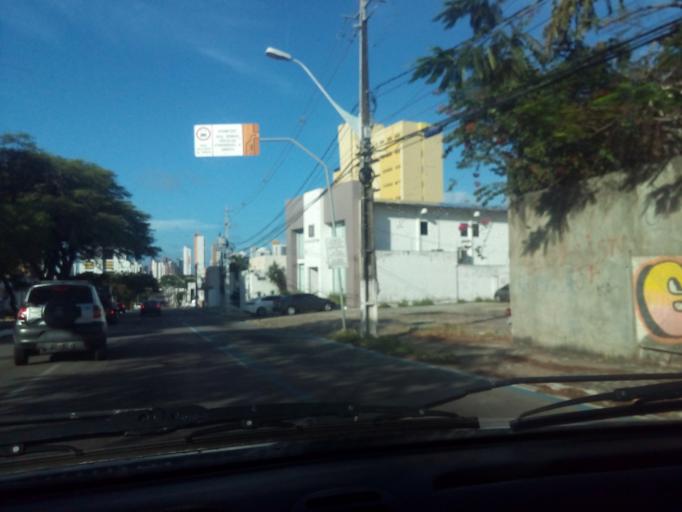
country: BR
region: Rio Grande do Norte
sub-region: Natal
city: Natal
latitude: -5.8002
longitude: -35.2004
